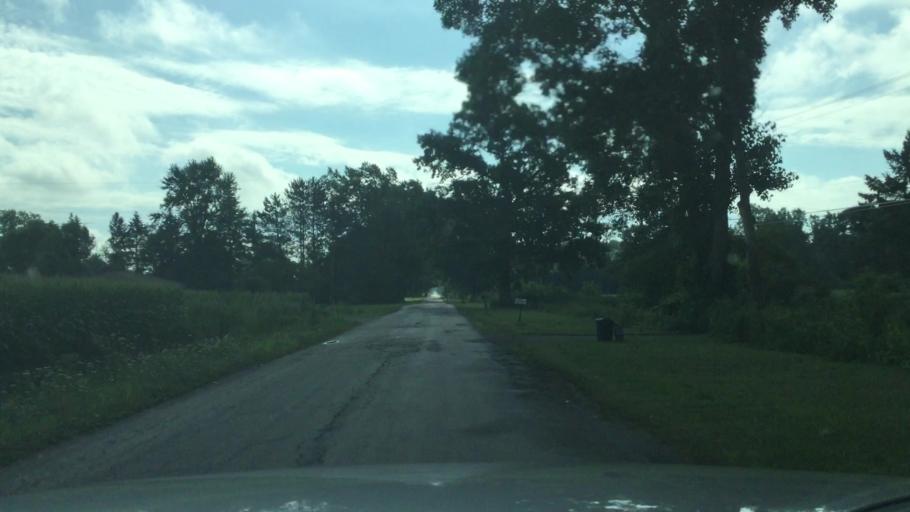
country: US
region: Michigan
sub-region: Genesee County
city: Clio
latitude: 43.2214
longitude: -83.7282
